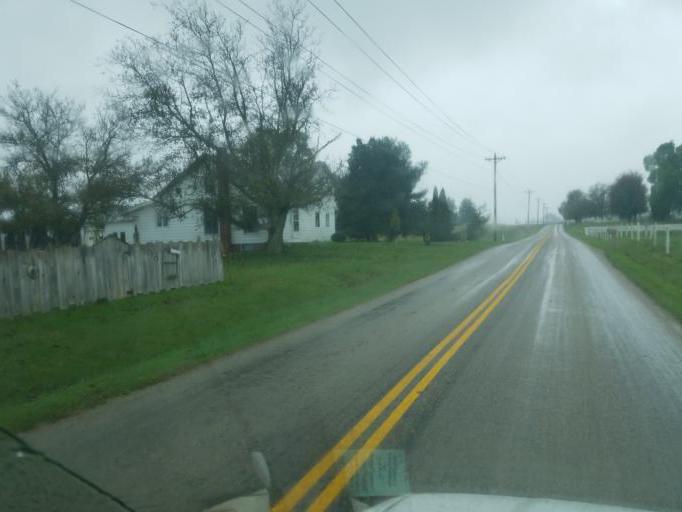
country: US
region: Ohio
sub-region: Wayne County
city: Shreve
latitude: 40.6280
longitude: -81.9772
